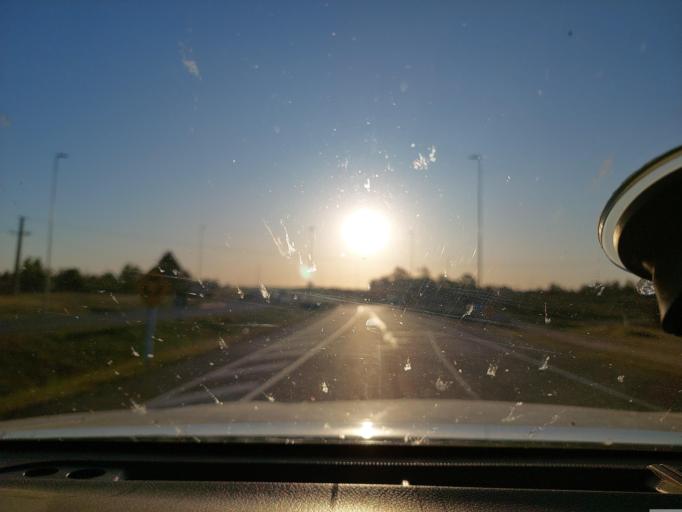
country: UY
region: Canelones
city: Empalme Olmos
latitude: -34.7011
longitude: -55.9188
